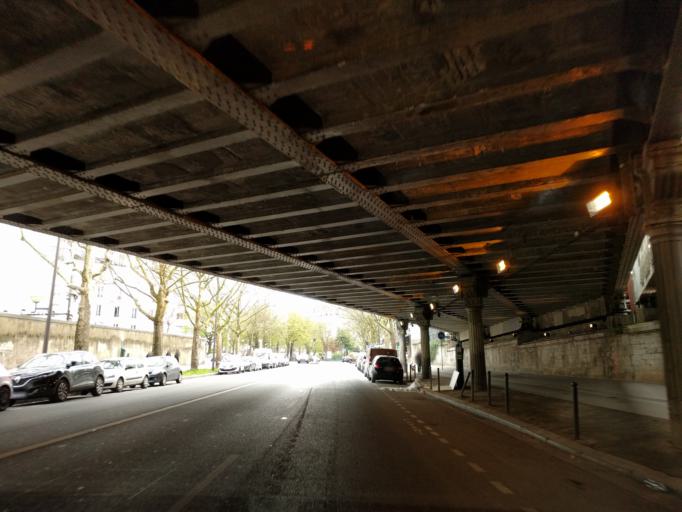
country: FR
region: Ile-de-France
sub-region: Departement du Val-de-Marne
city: Ivry-sur-Seine
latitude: 48.8391
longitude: 2.3862
